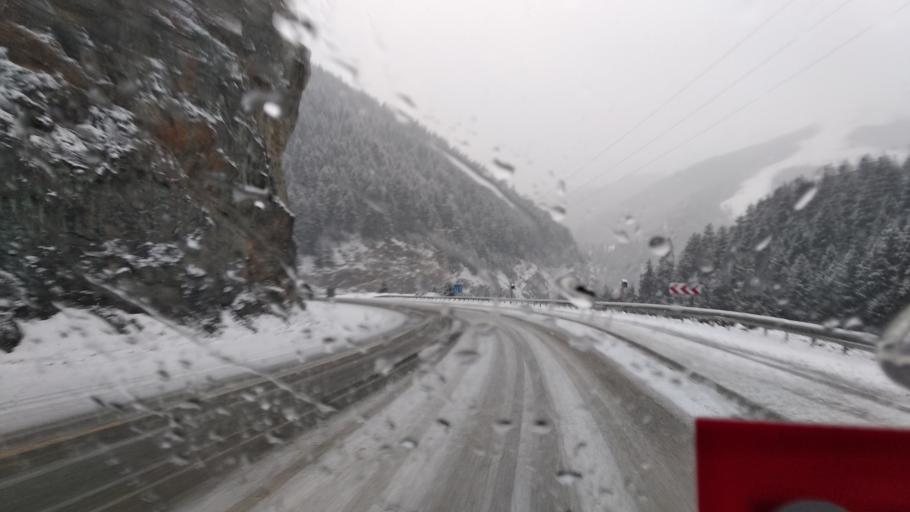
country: TR
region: Gumushane
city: Yaglidere
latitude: 40.6747
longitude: 39.4293
